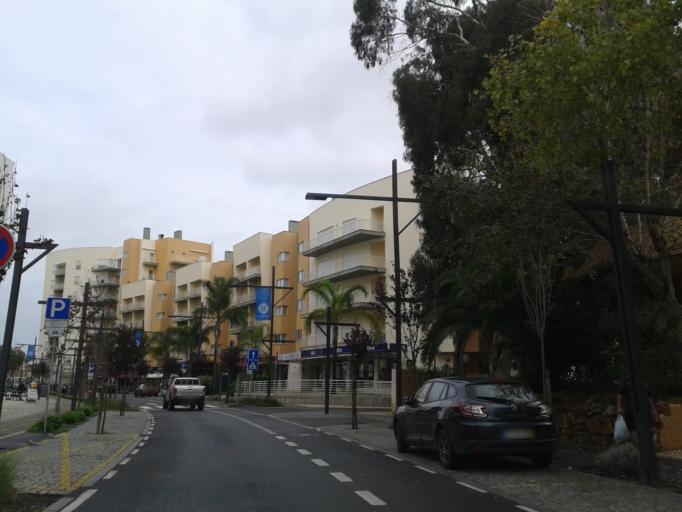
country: PT
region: Faro
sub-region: Loule
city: Vilamoura
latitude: 37.0752
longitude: -8.1152
